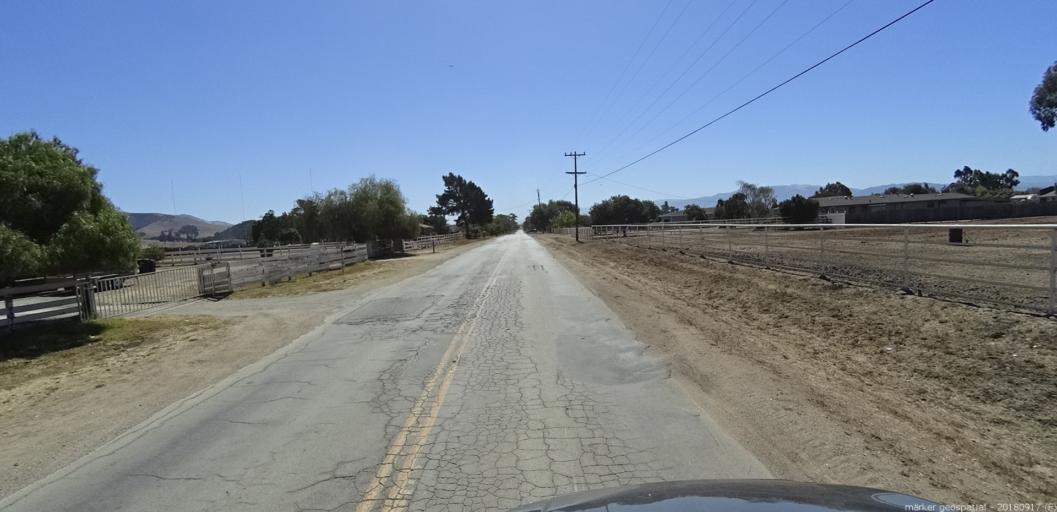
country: US
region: California
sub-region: Monterey County
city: Prunedale
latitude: 36.7361
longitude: -121.5992
